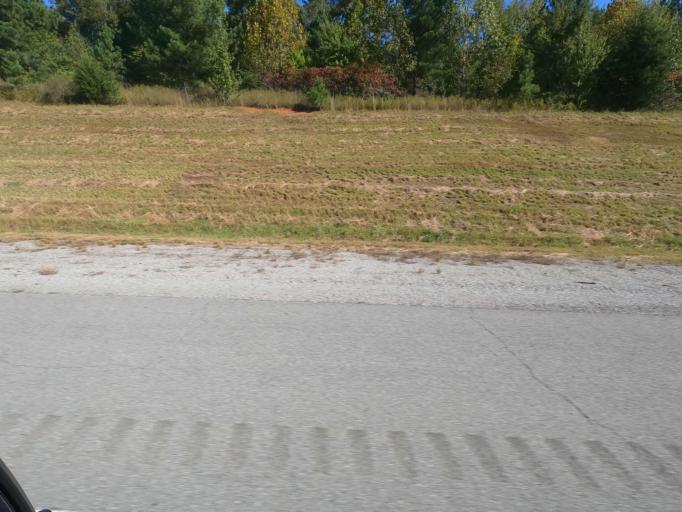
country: US
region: Tennessee
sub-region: Williamson County
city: Fairview
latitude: 35.9237
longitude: -87.1748
